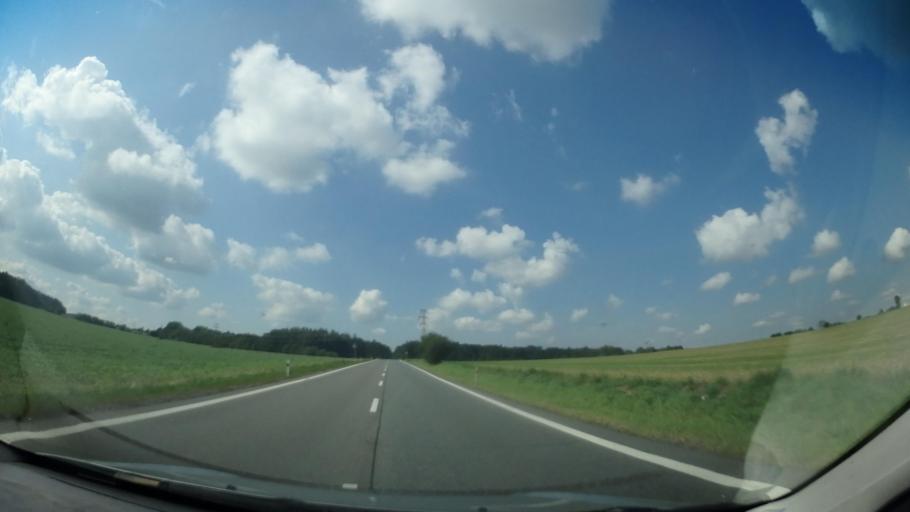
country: CZ
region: Central Bohemia
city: Kostelec nad Cernymi Lesy
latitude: 49.9826
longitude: 14.8821
